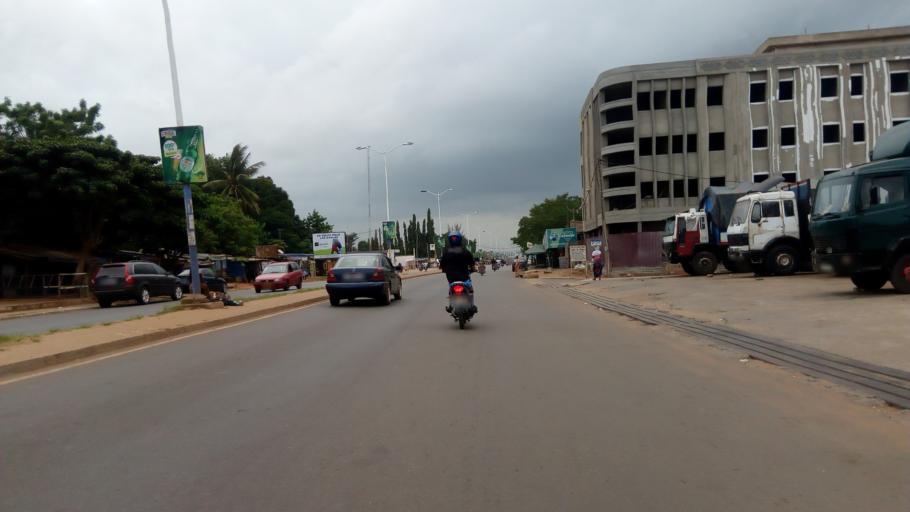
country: TG
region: Maritime
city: Lome
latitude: 6.2325
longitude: 1.2106
